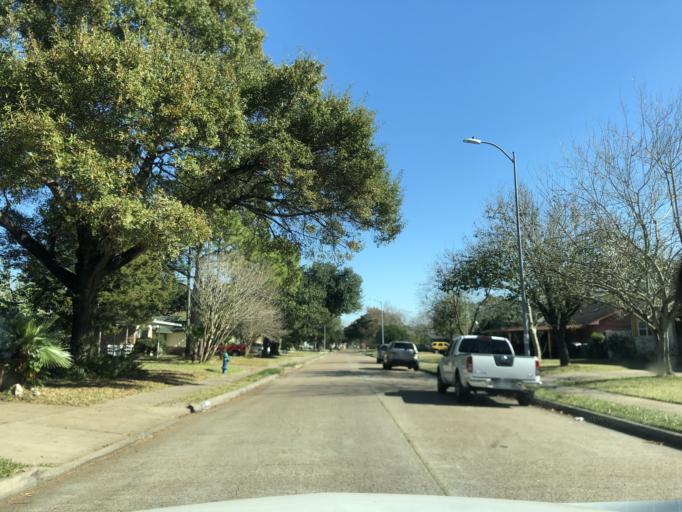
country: US
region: Texas
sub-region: Harris County
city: Bellaire
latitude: 29.6987
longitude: -95.5099
